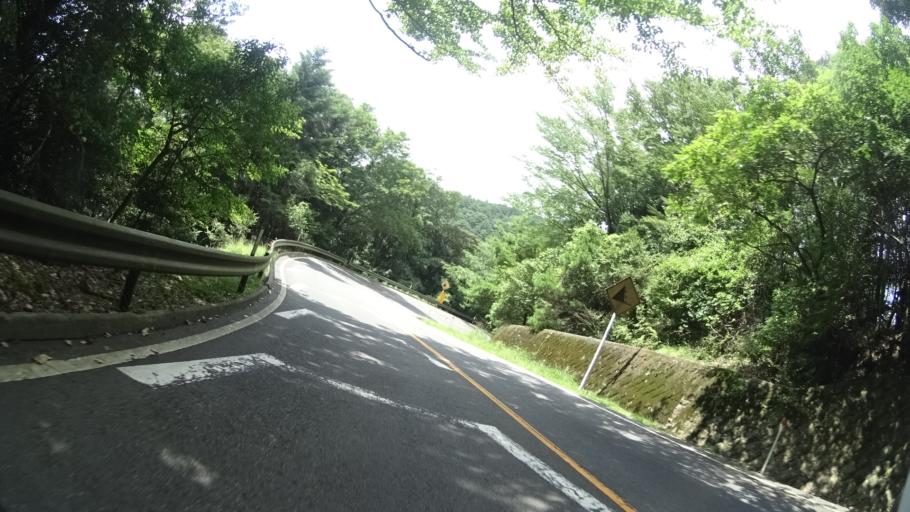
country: JP
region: Miyazaki
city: Kobayashi
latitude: 31.9035
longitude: 130.8468
